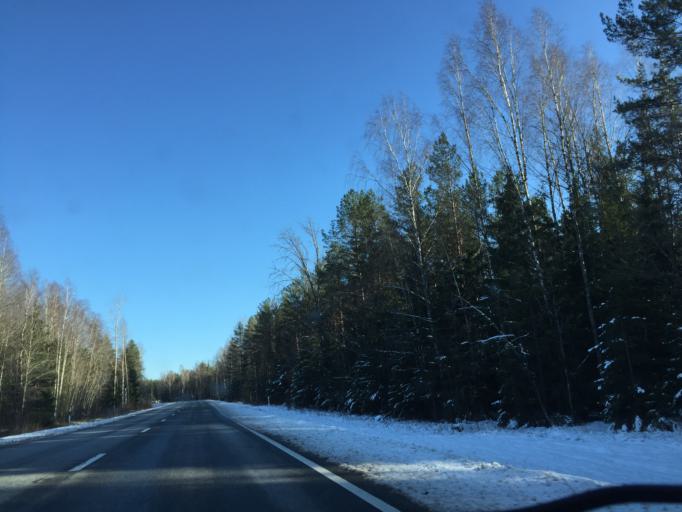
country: LV
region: Dundaga
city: Dundaga
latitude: 57.2499
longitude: 22.1643
